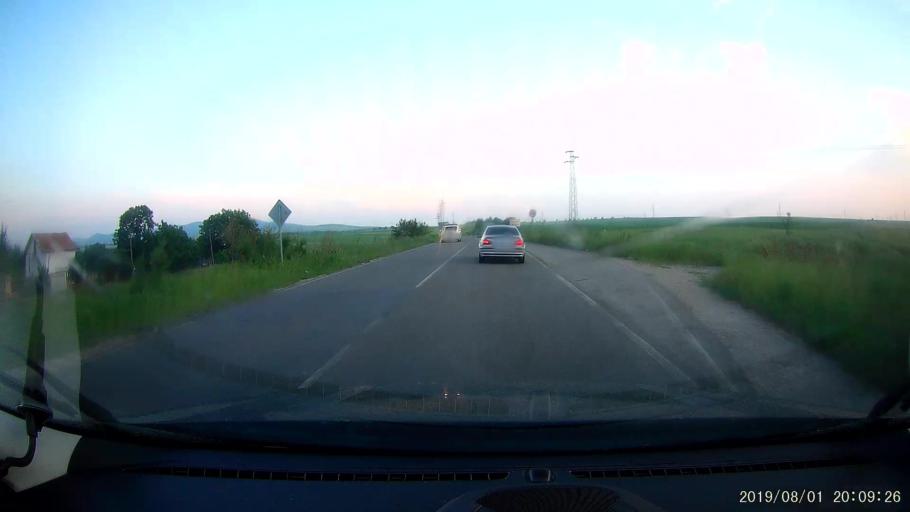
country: BG
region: Yambol
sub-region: Obshtina Yambol
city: Yambol
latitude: 42.4982
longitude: 26.5925
